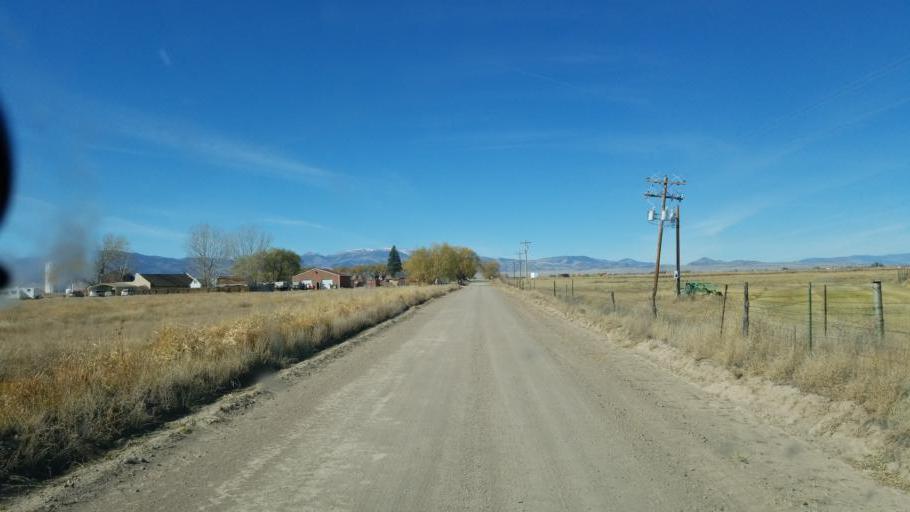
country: US
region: Colorado
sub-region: Rio Grande County
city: Monte Vista
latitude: 37.5313
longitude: -106.0541
